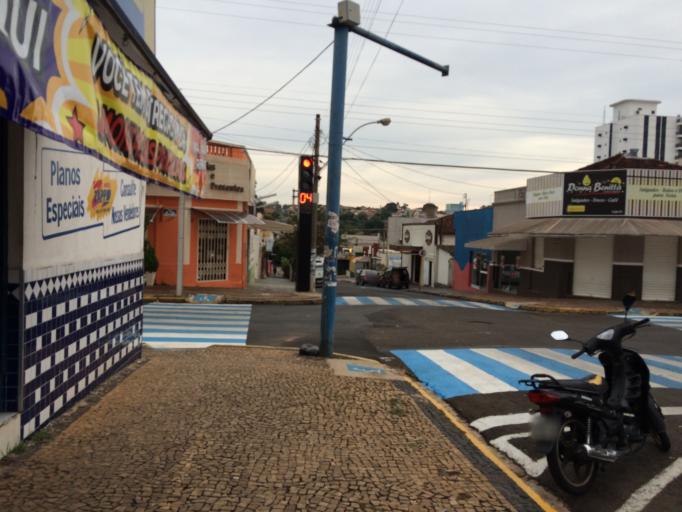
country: BR
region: Sao Paulo
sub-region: Matao
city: Matao
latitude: -21.6027
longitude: -48.3639
